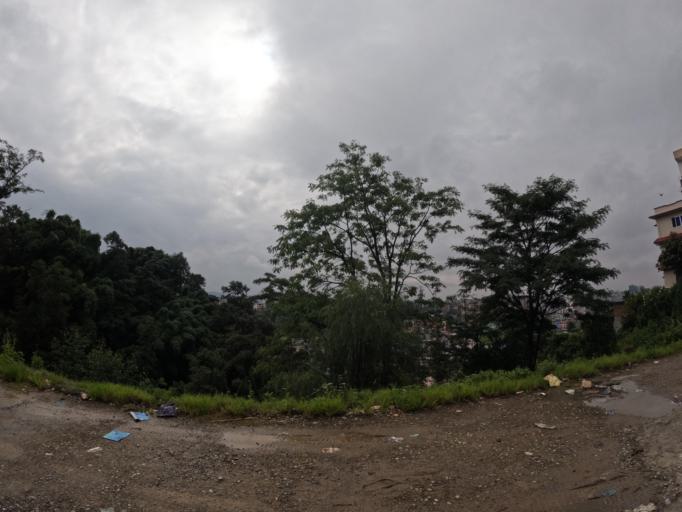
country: NP
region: Central Region
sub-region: Bagmati Zone
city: Kathmandu
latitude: 27.7597
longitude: 85.3233
